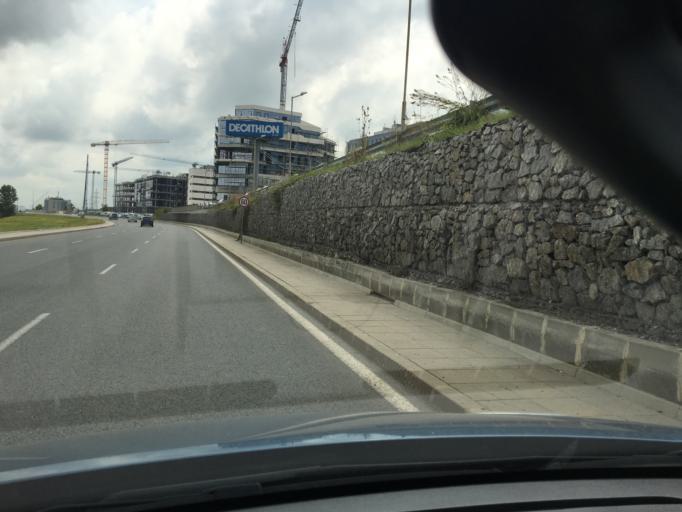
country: BG
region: Sofia-Capital
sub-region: Stolichna Obshtina
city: Sofia
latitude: 42.6235
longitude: 23.3661
